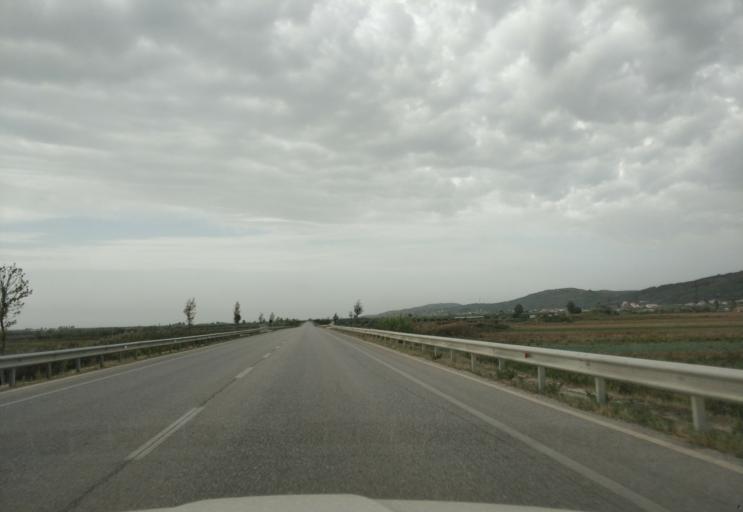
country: AL
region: Fier
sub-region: Rrethi i Fierit
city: Frakulla e Madhe
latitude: 40.6427
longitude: 19.5002
